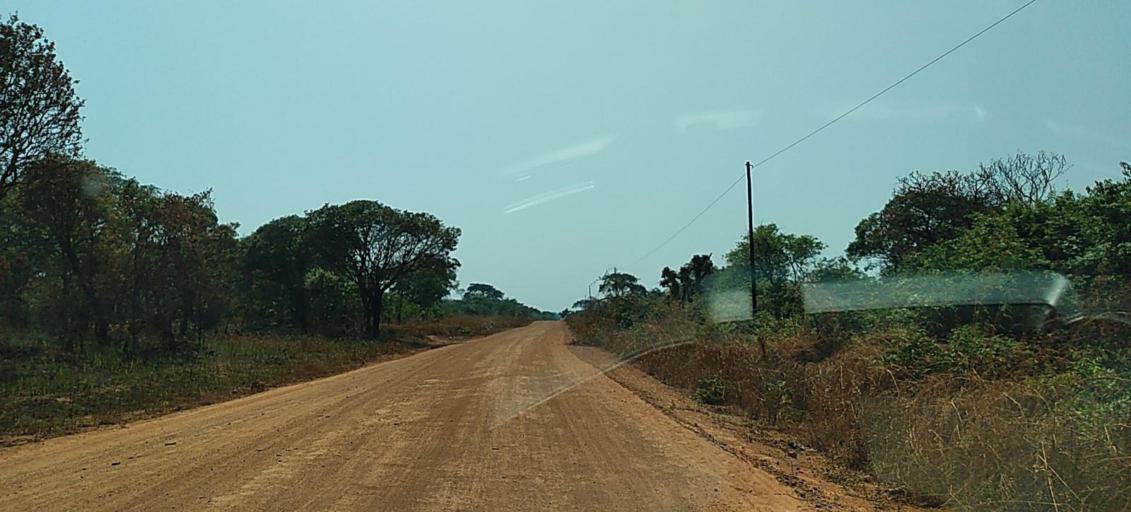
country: ZM
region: North-Western
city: Kansanshi
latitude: -11.9926
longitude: 26.6205
